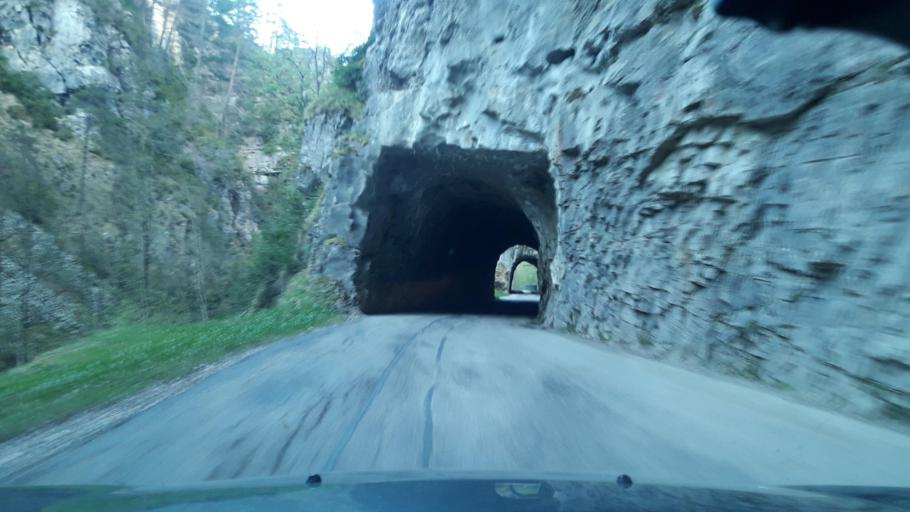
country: FR
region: Rhone-Alpes
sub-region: Departement de l'Isere
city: Mens
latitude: 44.6852
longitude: 5.5886
